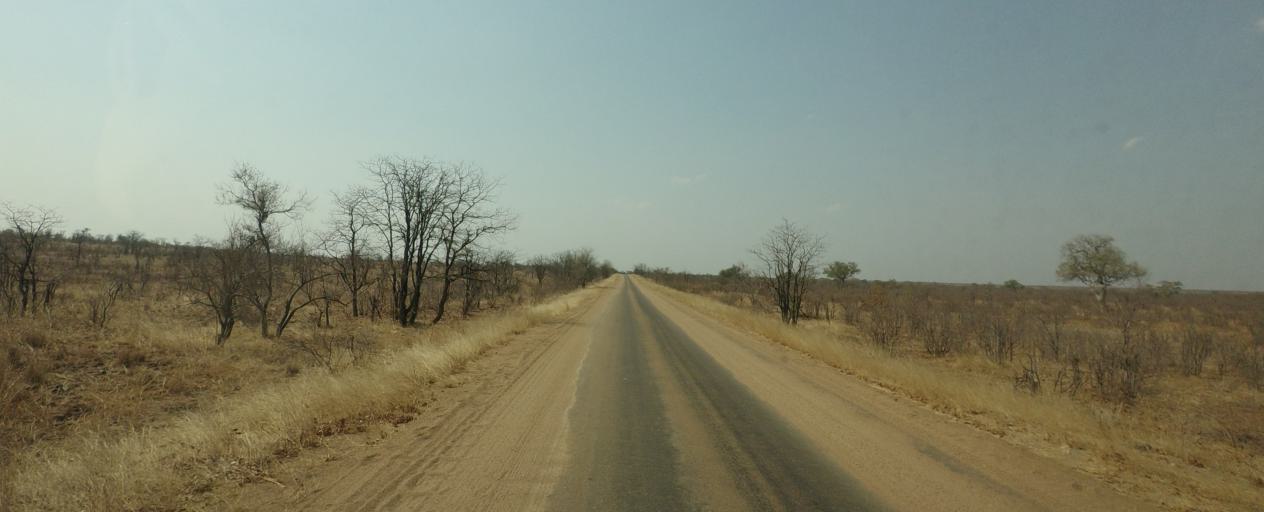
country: ZA
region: Limpopo
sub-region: Mopani District Municipality
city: Giyani
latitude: -23.2233
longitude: 31.3153
